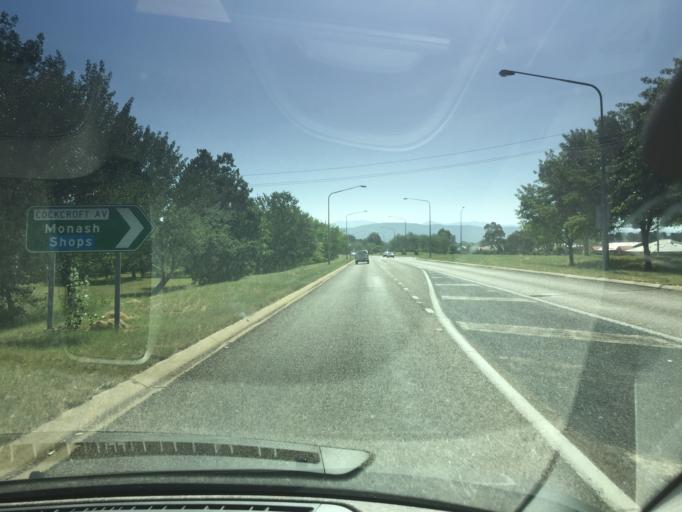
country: AU
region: Australian Capital Territory
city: Macarthur
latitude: -35.4213
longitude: 149.0992
